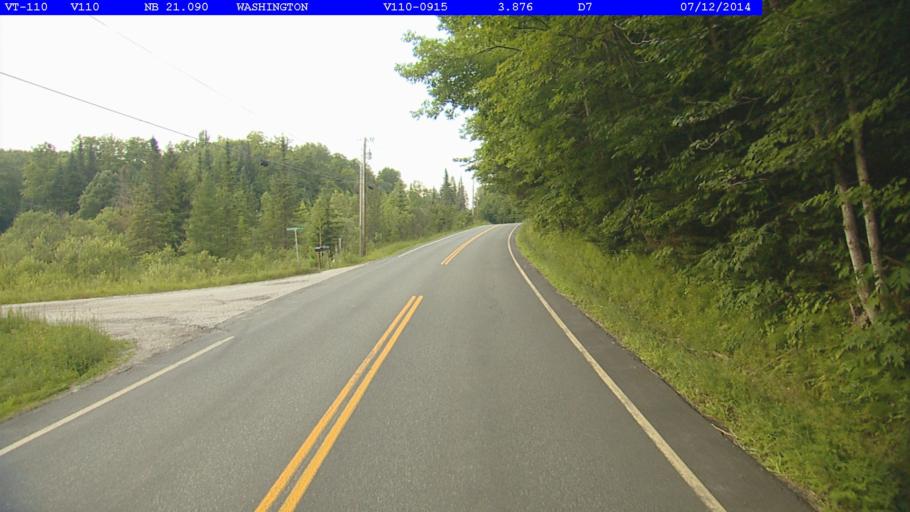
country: US
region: Vermont
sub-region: Orange County
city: Williamstown
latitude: 44.0902
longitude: -72.4587
